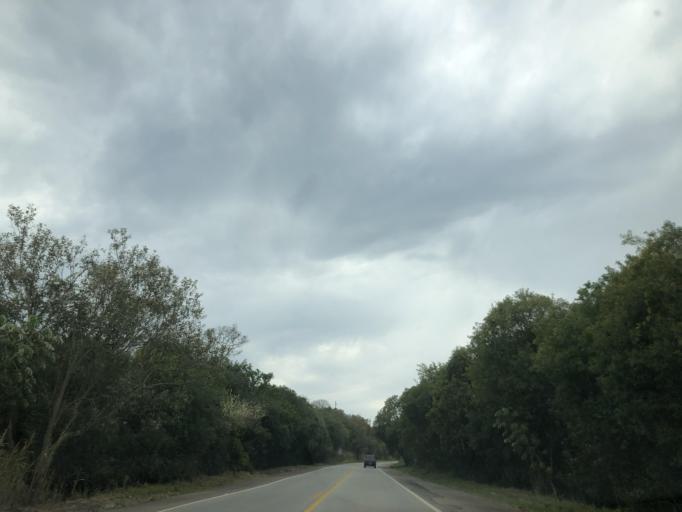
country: BR
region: Sao Paulo
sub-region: Salto De Pirapora
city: Salto de Pirapora
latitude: -23.7278
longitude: -47.6389
